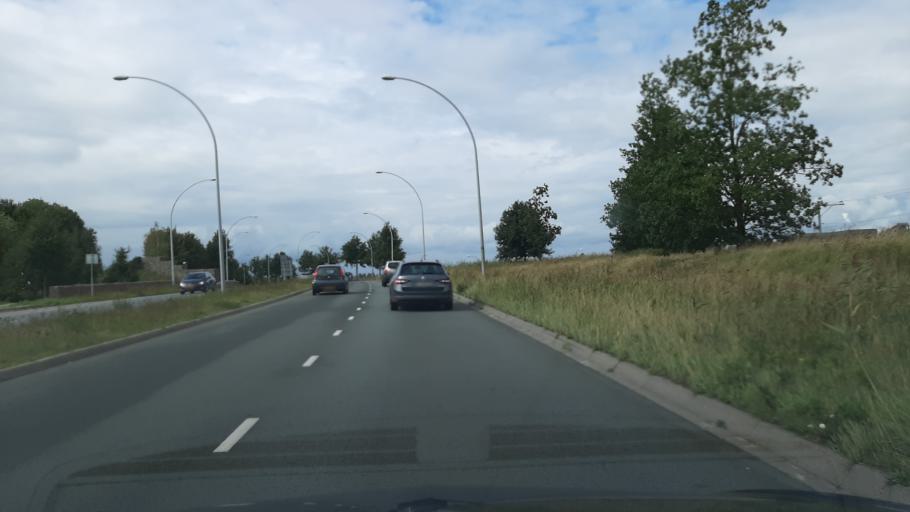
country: NL
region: Overijssel
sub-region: Gemeente Zwolle
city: Zwolle
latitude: 52.5265
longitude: 6.0527
